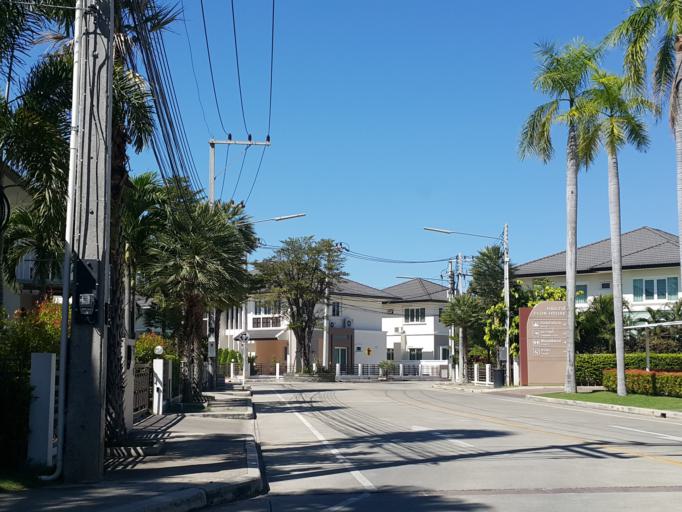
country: TH
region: Chiang Mai
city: San Sai
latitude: 18.8372
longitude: 99.0628
